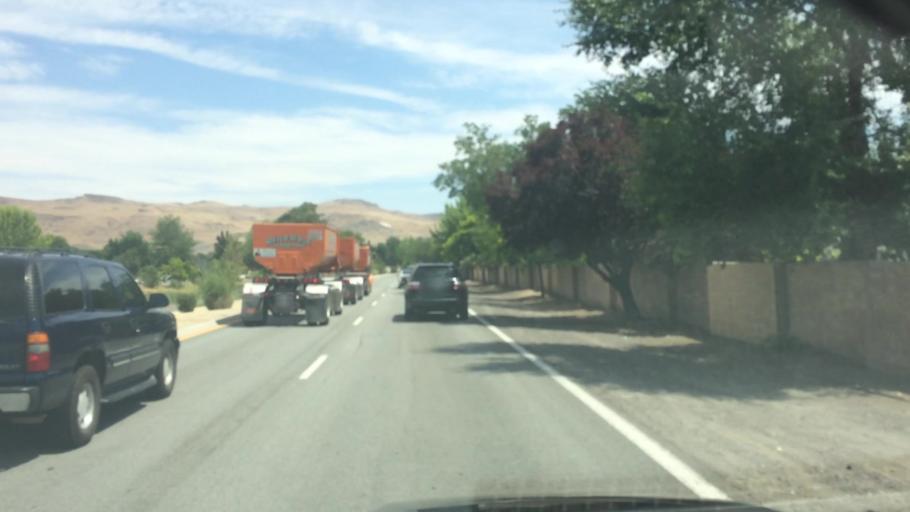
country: US
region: Nevada
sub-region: Washoe County
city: Sparks
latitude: 39.5504
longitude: -119.7178
